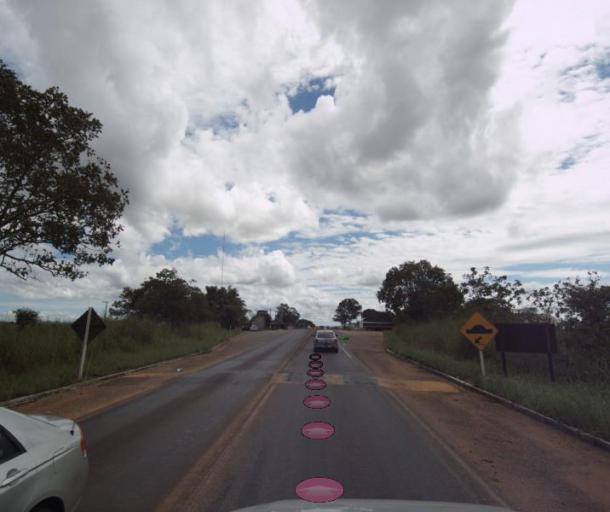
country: BR
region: Goias
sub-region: Uruacu
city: Uruacu
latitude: -14.4713
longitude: -49.1560
